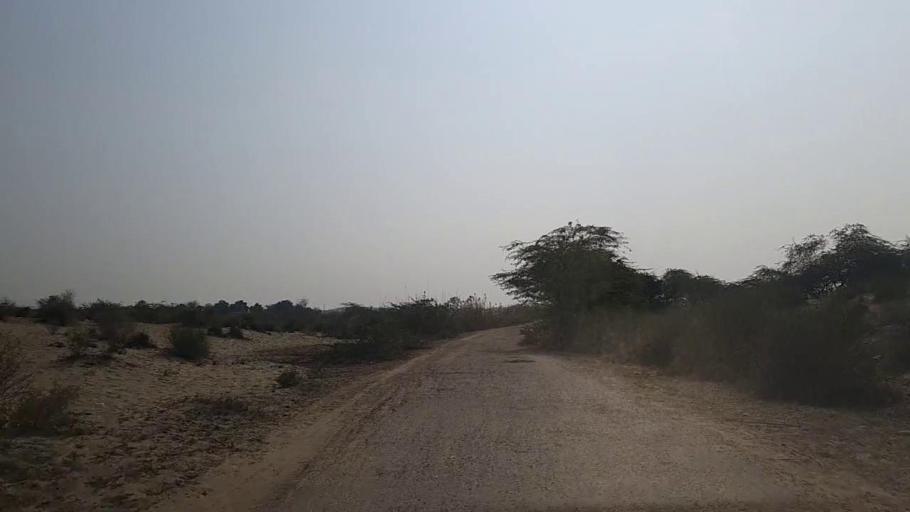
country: PK
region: Sindh
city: Jam Sahib
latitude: 26.4437
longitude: 68.5236
